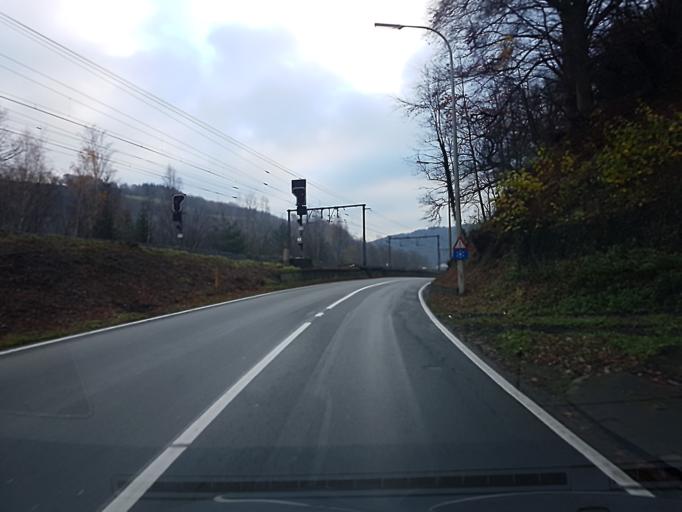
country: BE
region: Wallonia
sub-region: Province de Liege
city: Trooz
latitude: 50.5696
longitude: 5.6972
